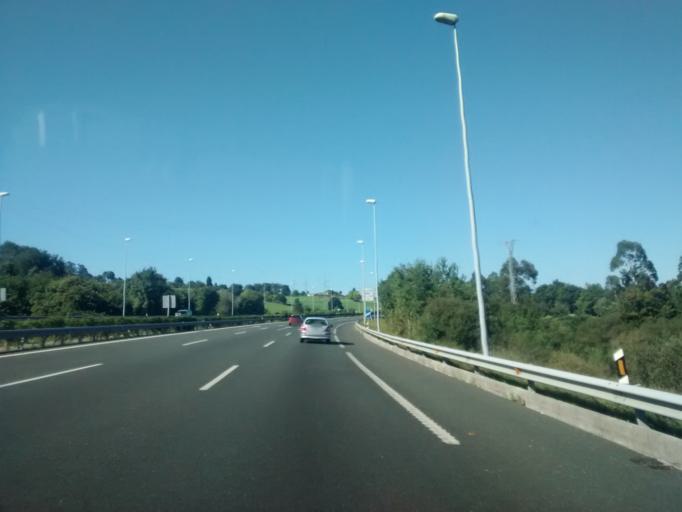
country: ES
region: Cantabria
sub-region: Provincia de Cantabria
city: Reocin
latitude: 43.3453
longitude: -4.1286
